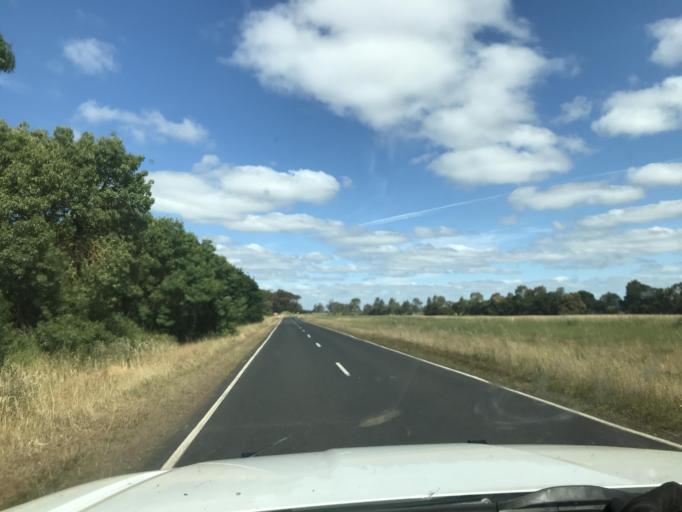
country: AU
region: South Australia
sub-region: Naracoorte and Lucindale
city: Naracoorte
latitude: -37.0181
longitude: 141.3021
